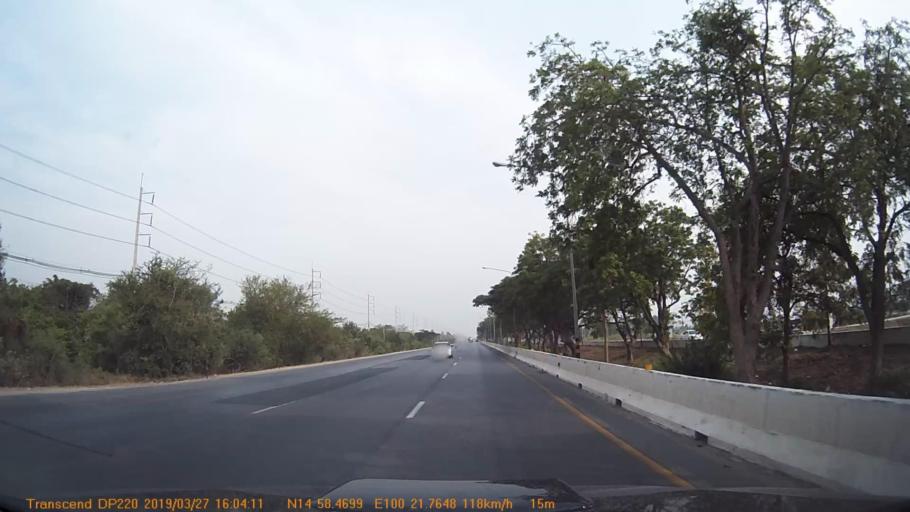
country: TH
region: Sing Buri
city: In Buri
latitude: 14.9742
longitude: 100.3630
